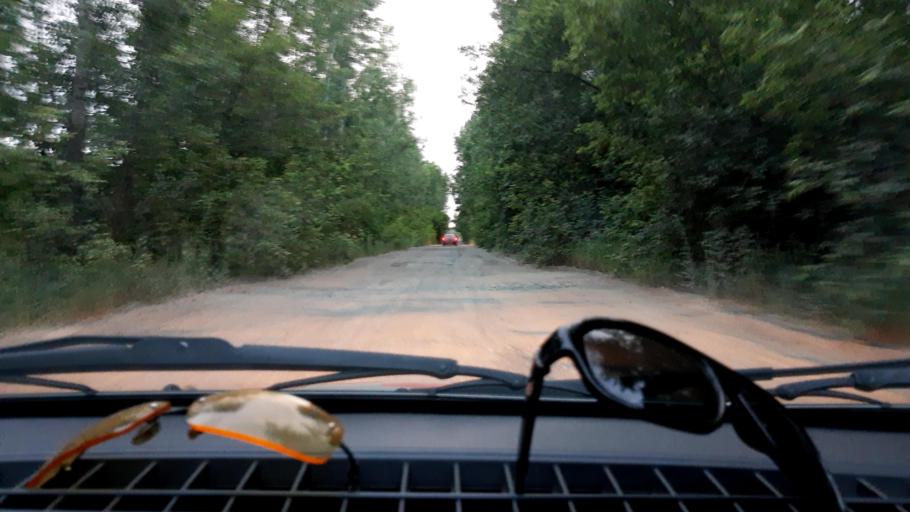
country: RU
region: Bashkortostan
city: Avdon
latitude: 54.6605
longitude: 55.8210
